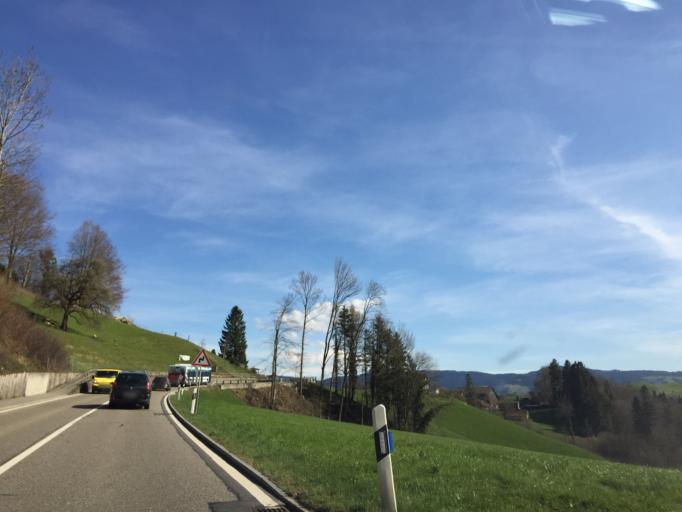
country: CH
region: Zurich
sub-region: Bezirk Horgen
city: Horgen / Allmend
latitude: 47.2132
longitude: 8.5991
